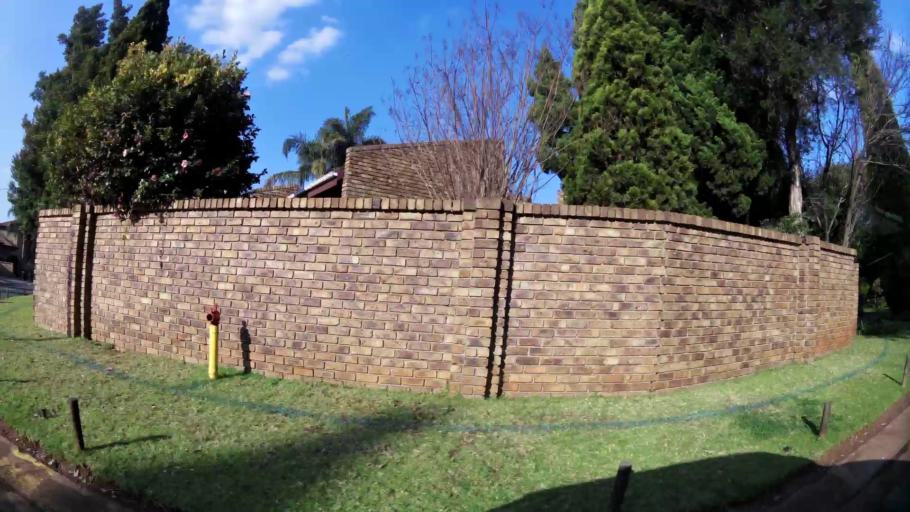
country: ZA
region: Gauteng
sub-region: City of Johannesburg Metropolitan Municipality
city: Modderfontein
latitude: -26.0743
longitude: 28.2044
